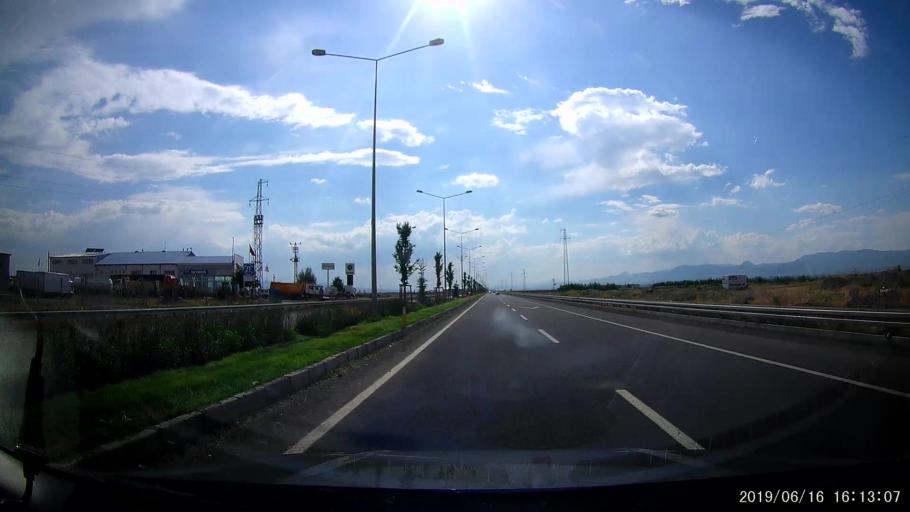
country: TR
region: Erzurum
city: Erzurum
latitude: 39.9592
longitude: 41.2782
